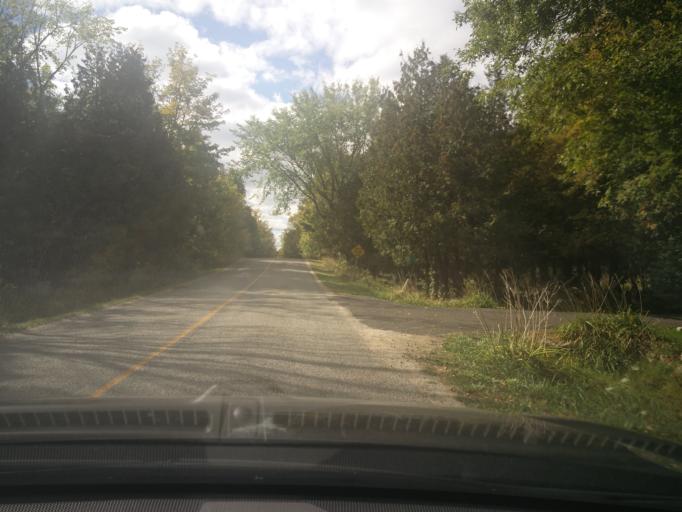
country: CA
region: Ontario
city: Perth
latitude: 44.6579
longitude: -76.5492
